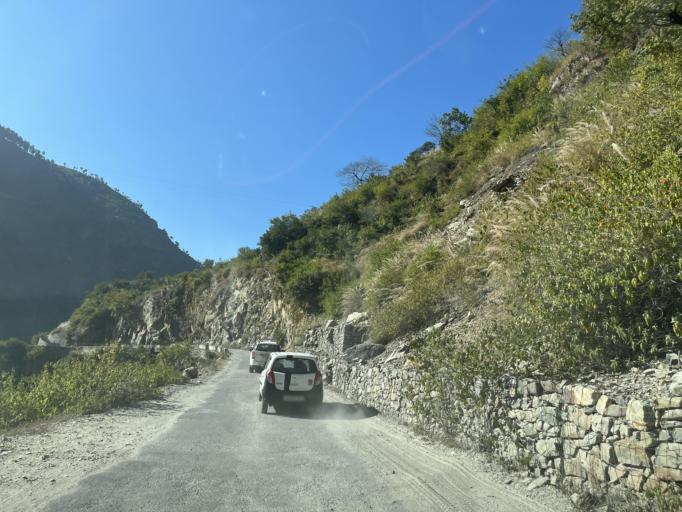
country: IN
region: Uttarakhand
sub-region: Naini Tal
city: Naini Tal
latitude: 29.5105
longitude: 79.4661
